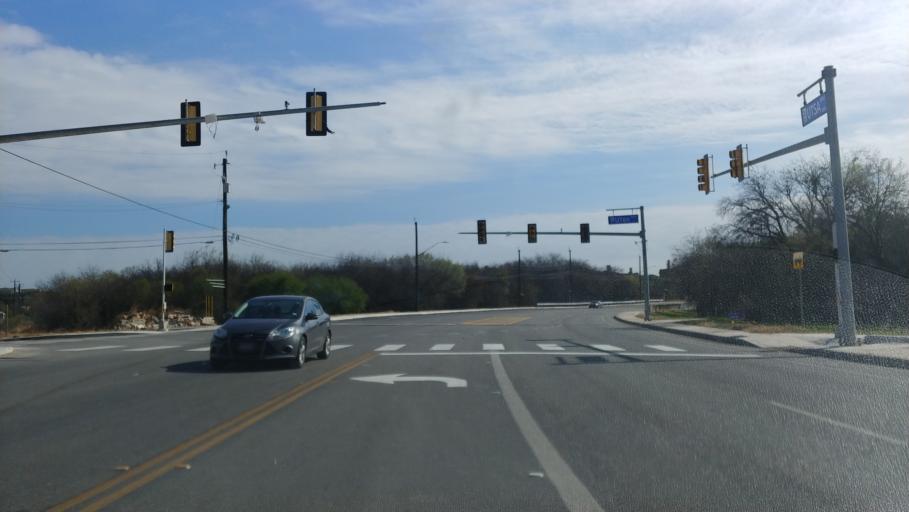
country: US
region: Texas
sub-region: Bexar County
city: Shavano Park
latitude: 29.5789
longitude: -98.6043
